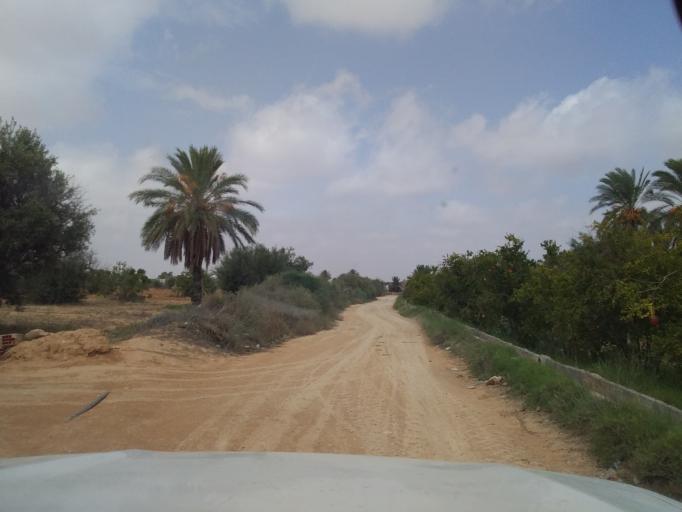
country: TN
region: Qabis
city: Gabes
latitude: 33.6265
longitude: 10.3081
